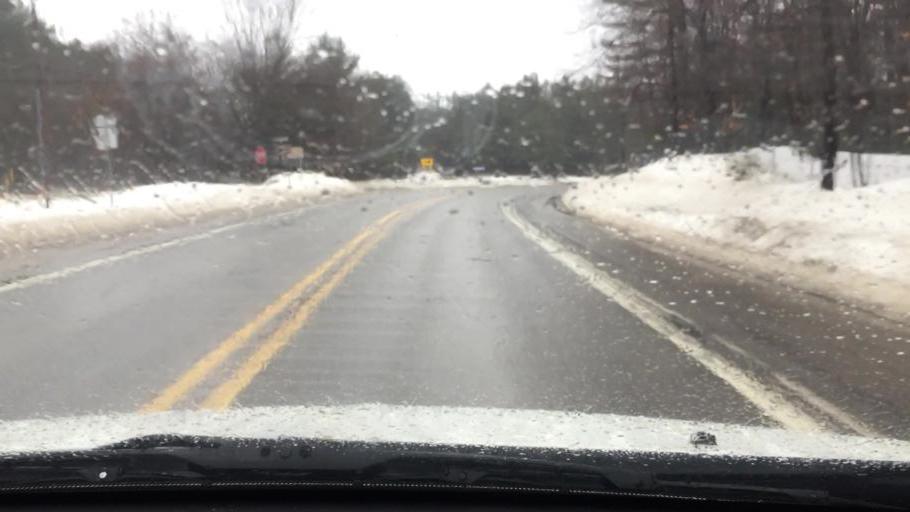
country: US
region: Michigan
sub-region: Charlevoix County
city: East Jordan
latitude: 45.2276
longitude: -85.1812
